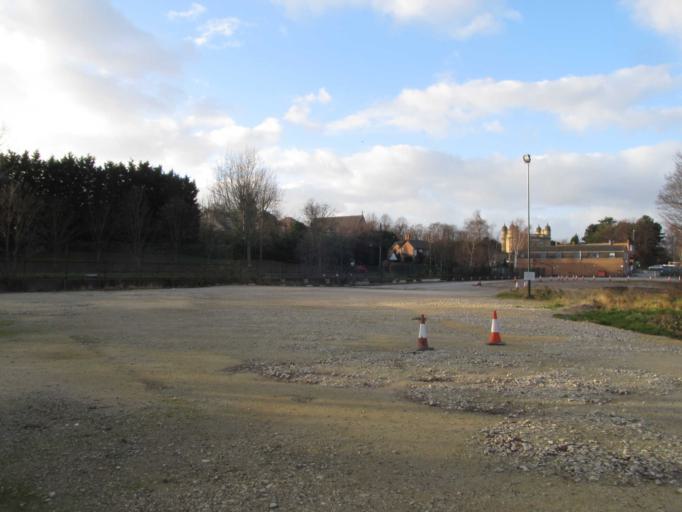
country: GB
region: England
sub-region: Nottingham
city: Nottingham
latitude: 52.9459
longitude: -1.1827
